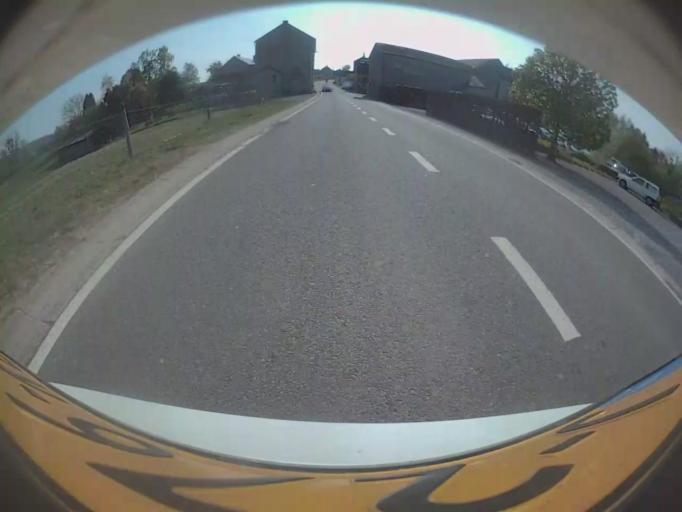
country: BE
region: Wallonia
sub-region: Province de Namur
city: Havelange
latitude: 50.3301
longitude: 5.2633
